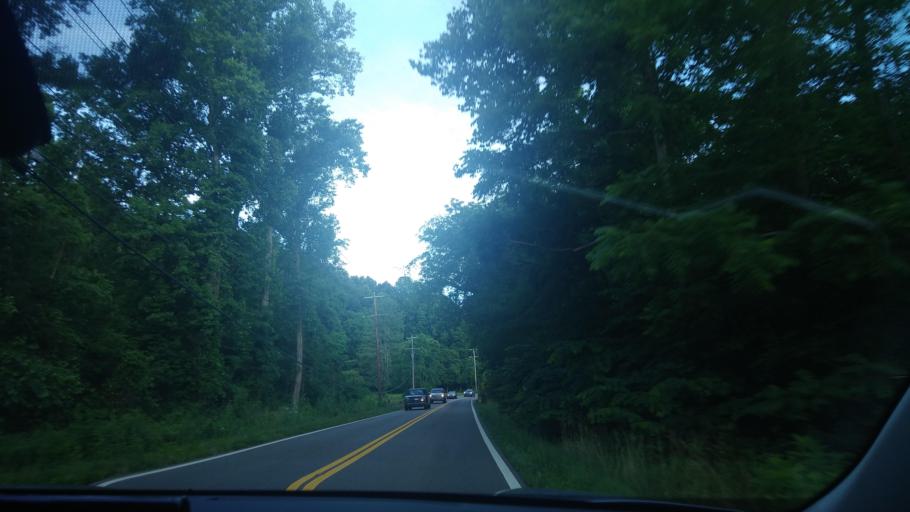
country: US
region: Tennessee
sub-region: Cocke County
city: Newport
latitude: 35.8032
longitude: -83.2460
